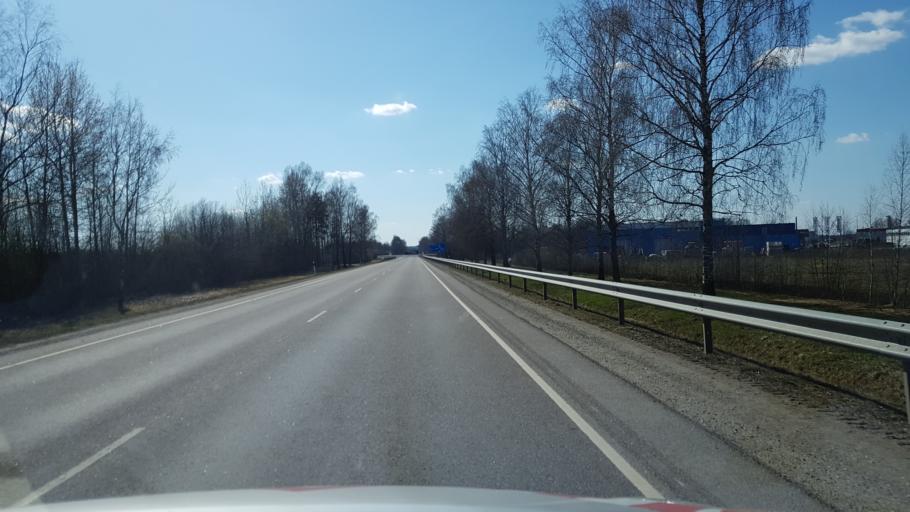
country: EE
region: Tartu
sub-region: Tartu linn
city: Tartu
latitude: 58.4127
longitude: 26.7281
